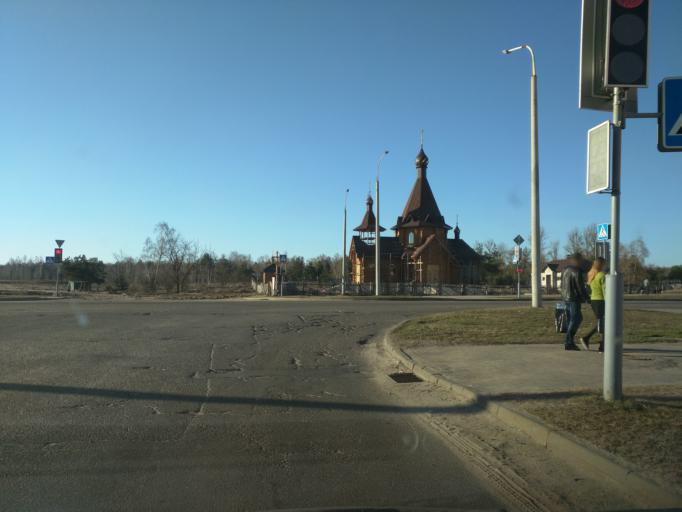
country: BY
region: Mogilev
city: Babruysk
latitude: 53.1672
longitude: 29.1638
